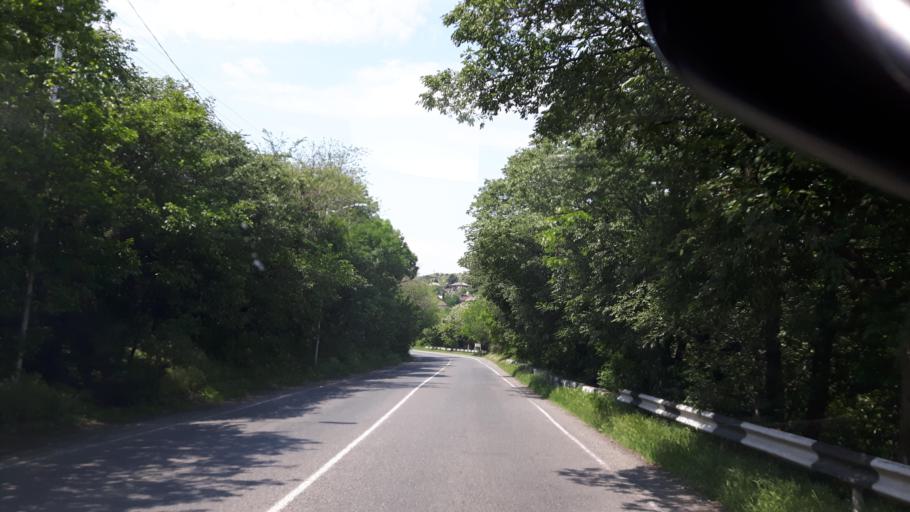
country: GE
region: Mtskheta-Mtianeti
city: Mtskheta
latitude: 41.8397
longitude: 44.7199
